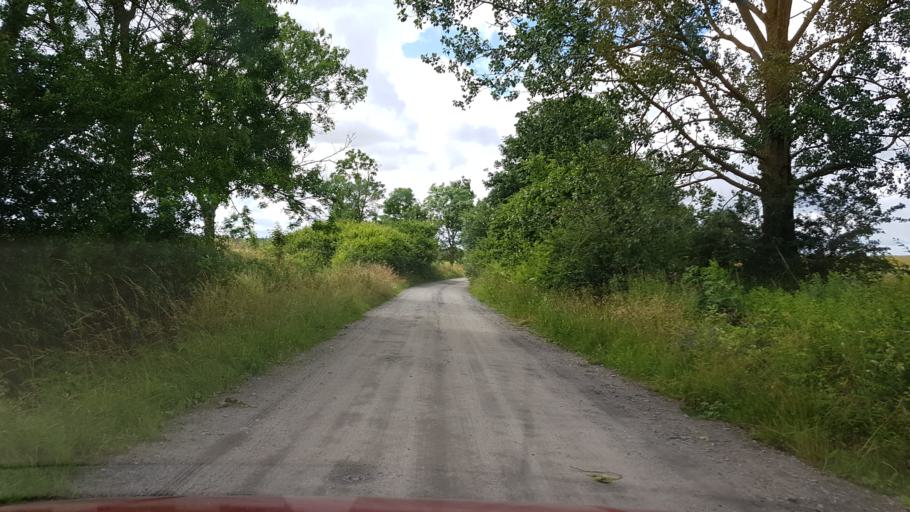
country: PL
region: West Pomeranian Voivodeship
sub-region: Powiat koszalinski
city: Mielno
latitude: 54.1680
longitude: 15.9621
